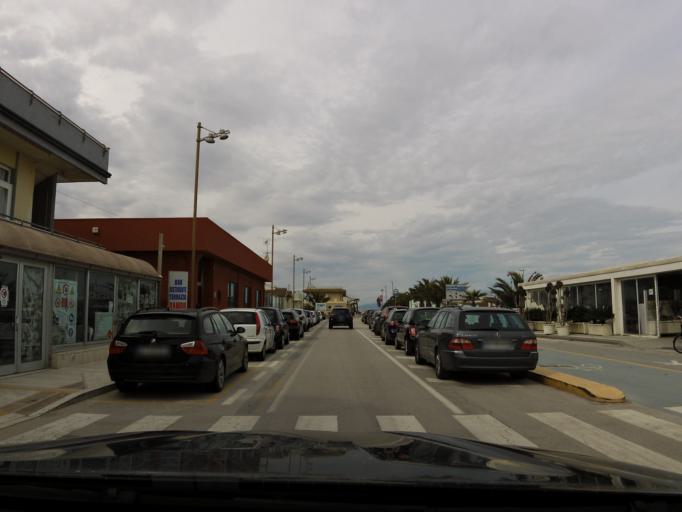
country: IT
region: The Marches
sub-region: Provincia di Macerata
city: Civitanova Marche
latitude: 43.3281
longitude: 13.7151
